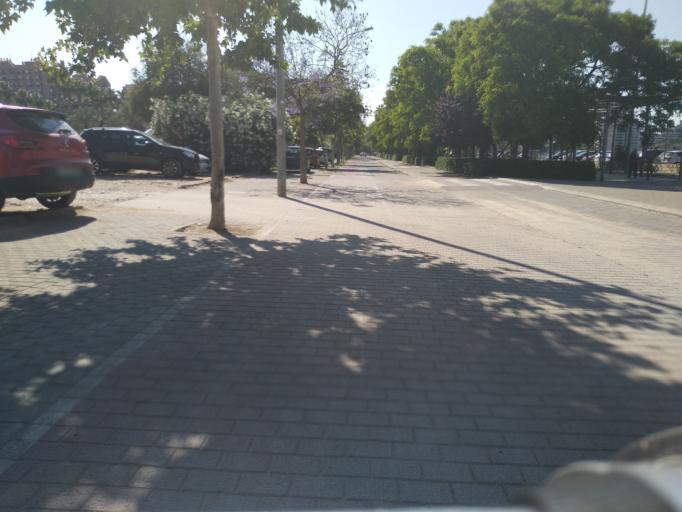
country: ES
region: Valencia
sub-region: Provincia de Valencia
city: Alboraya
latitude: 39.4786
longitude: -0.3481
